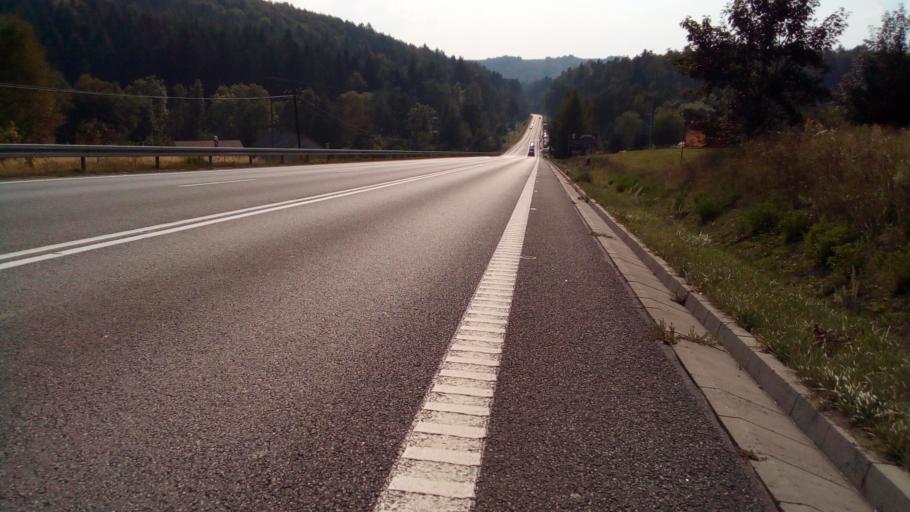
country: PL
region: Subcarpathian Voivodeship
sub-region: Powiat strzyzowski
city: Jawornik
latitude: 49.8338
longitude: 21.8854
